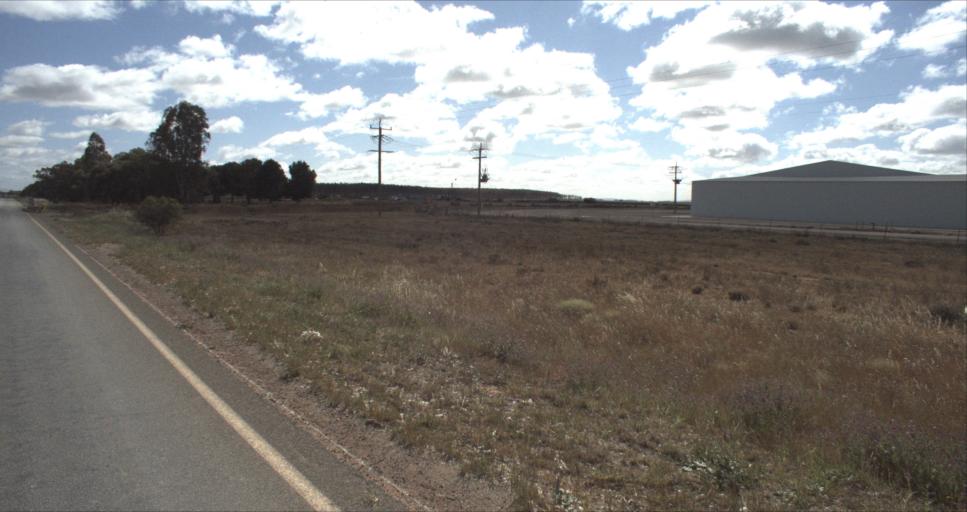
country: AU
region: New South Wales
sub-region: Murrumbidgee Shire
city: Darlington Point
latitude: -34.5933
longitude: 146.1632
